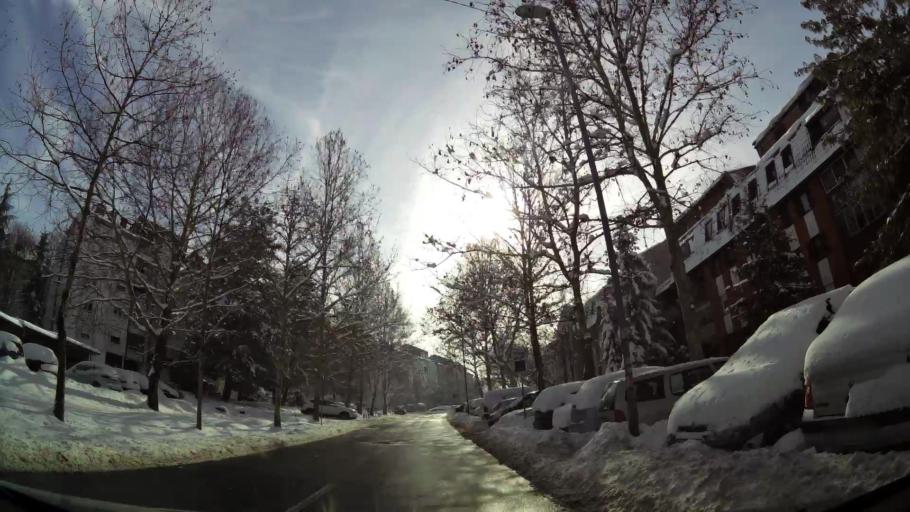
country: RS
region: Central Serbia
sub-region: Belgrade
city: Zvezdara
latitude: 44.7898
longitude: 20.5408
